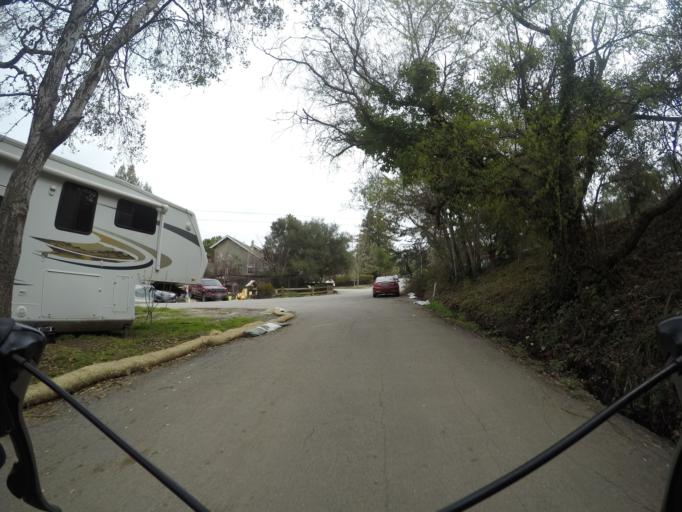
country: US
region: California
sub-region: Santa Cruz County
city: Scotts Valley
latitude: 37.0609
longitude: -121.9971
